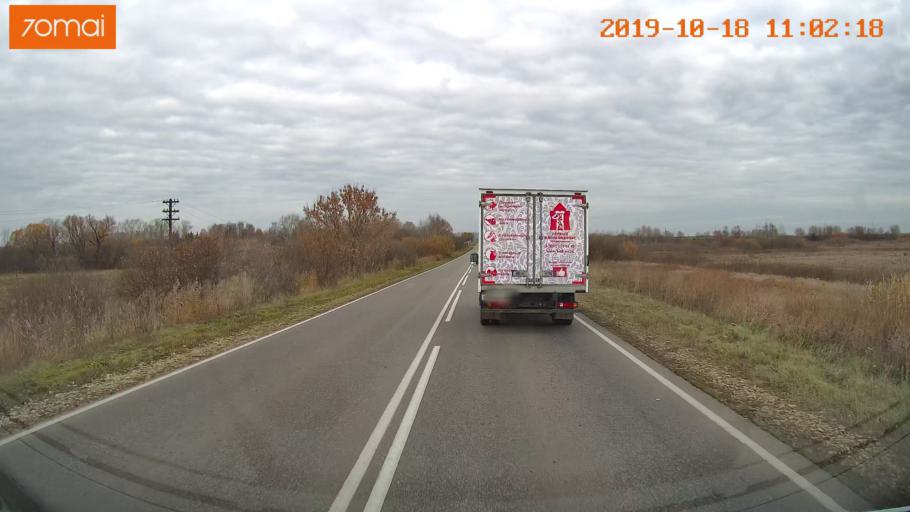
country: RU
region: Tula
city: Yepifan'
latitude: 53.8636
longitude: 38.5452
